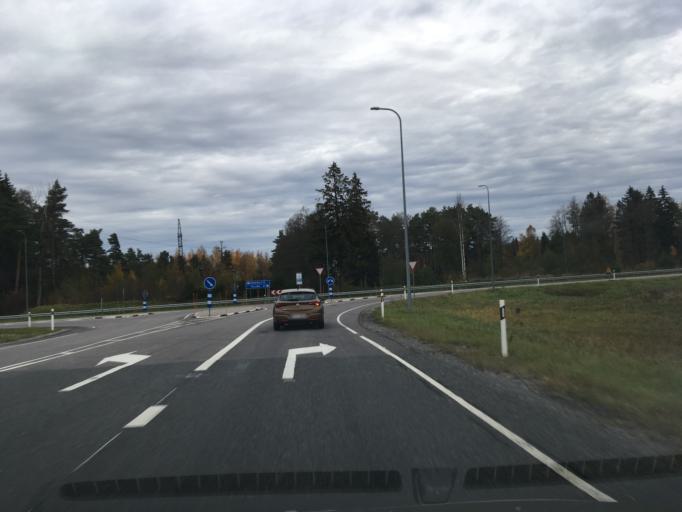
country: EE
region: Harju
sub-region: Nissi vald
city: Turba
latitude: 58.9930
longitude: 24.0586
